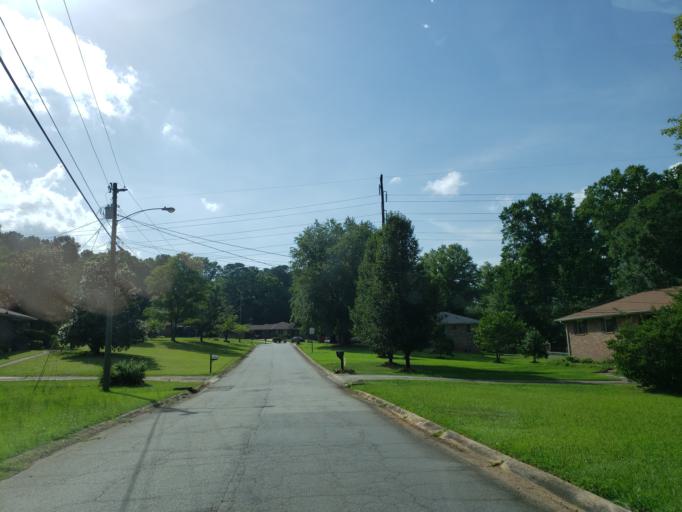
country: US
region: Georgia
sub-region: Cobb County
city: Austell
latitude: 33.8713
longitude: -84.6191
